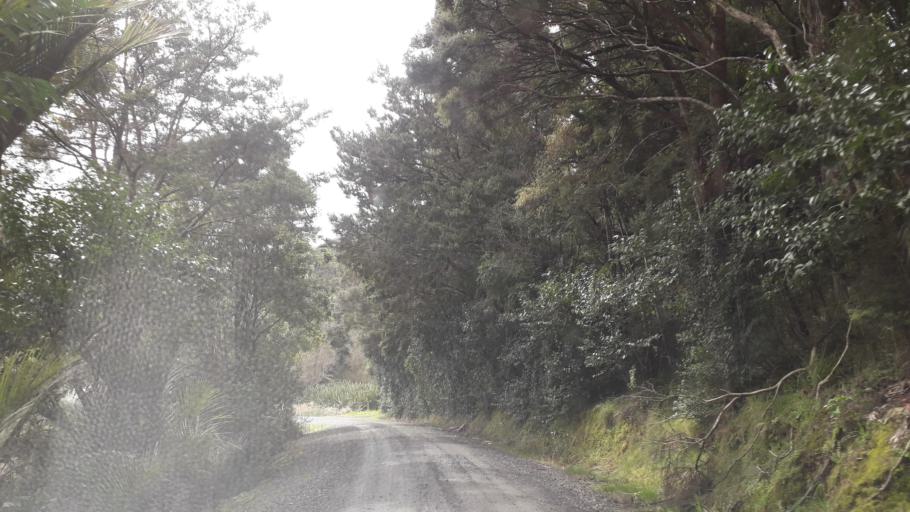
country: NZ
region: Northland
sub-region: Far North District
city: Waimate North
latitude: -35.3079
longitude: 173.5639
